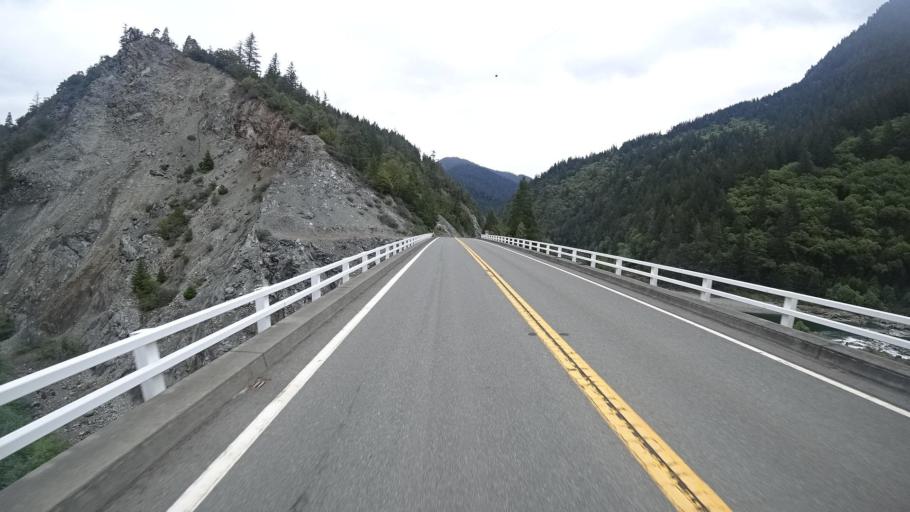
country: US
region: California
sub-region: Humboldt County
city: Willow Creek
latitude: 41.2410
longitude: -123.6550
